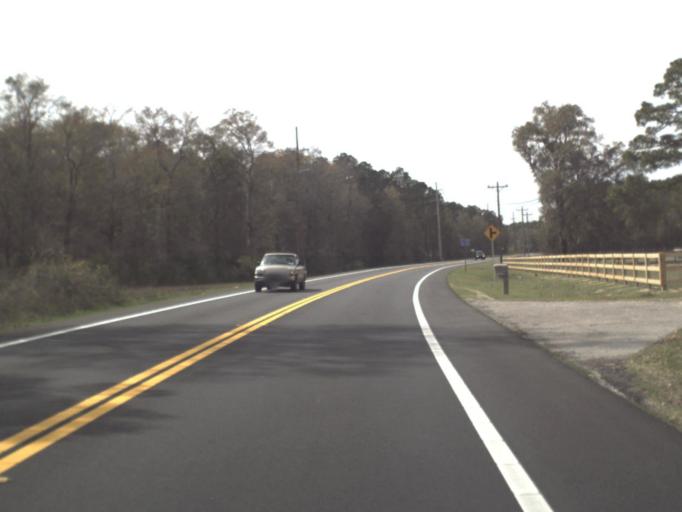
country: US
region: Florida
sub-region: Gadsden County
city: Midway
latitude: 30.4389
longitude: -84.4726
